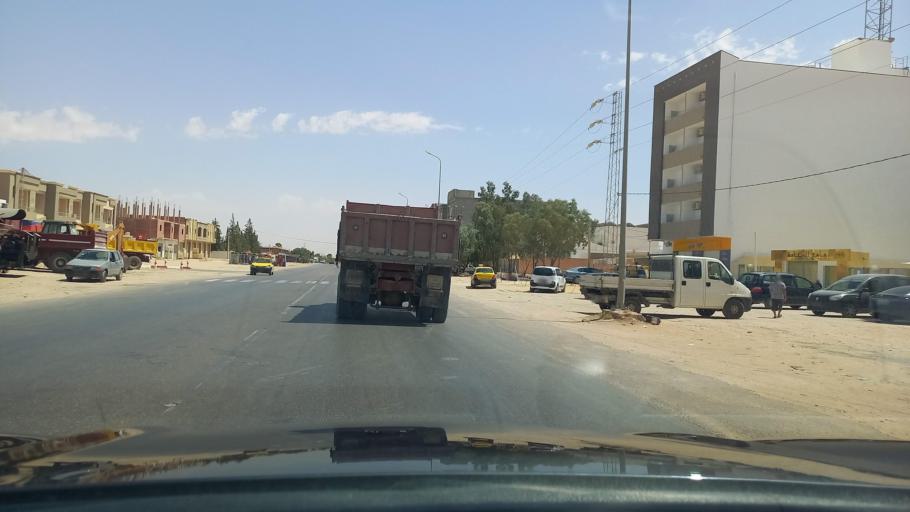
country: TN
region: Madanin
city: Medenine
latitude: 33.3652
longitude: 10.4593
